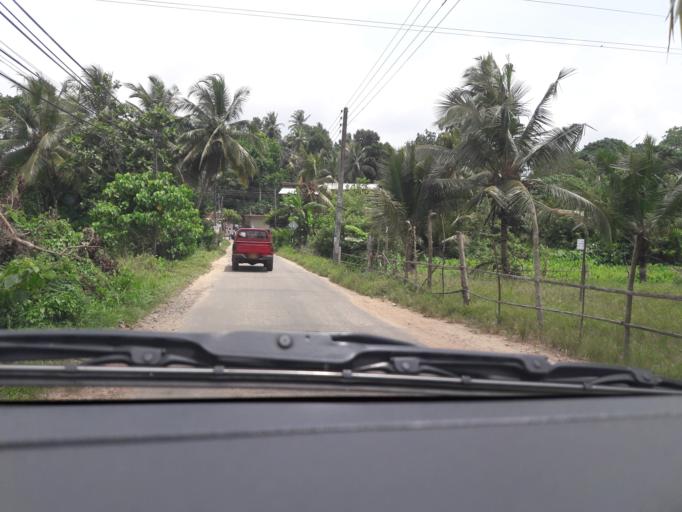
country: LK
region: Southern
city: Unawatuna
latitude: 6.0487
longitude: 80.2499
